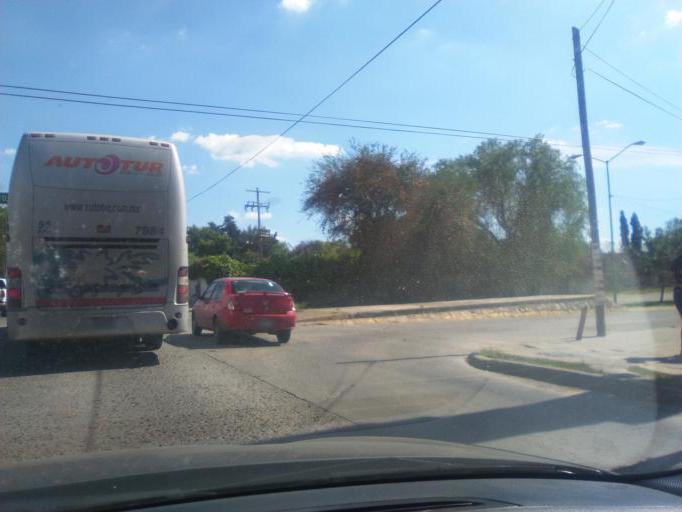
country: MX
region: Guanajuato
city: Leon
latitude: 21.1077
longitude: -101.6430
